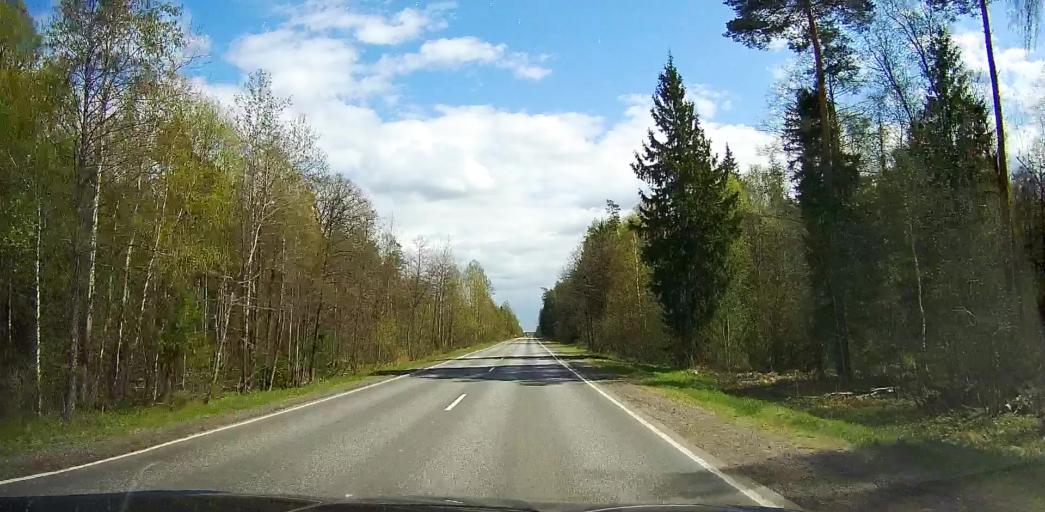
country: RU
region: Moskovskaya
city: Davydovo
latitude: 55.5513
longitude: 38.7720
